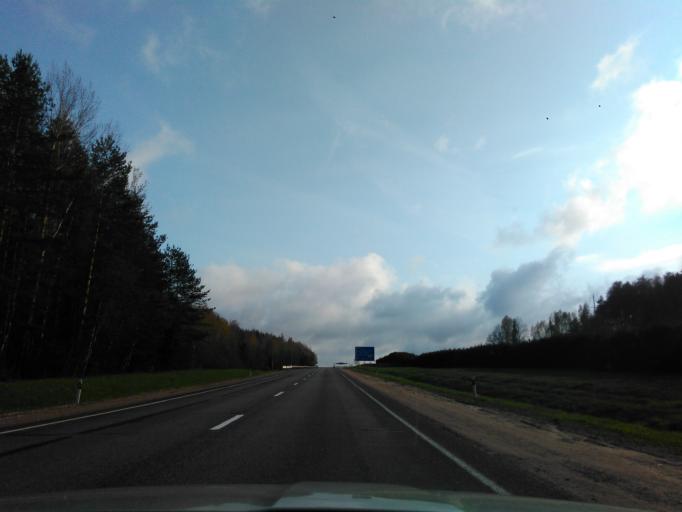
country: BY
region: Minsk
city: Lahoysk
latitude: 54.2153
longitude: 27.8293
